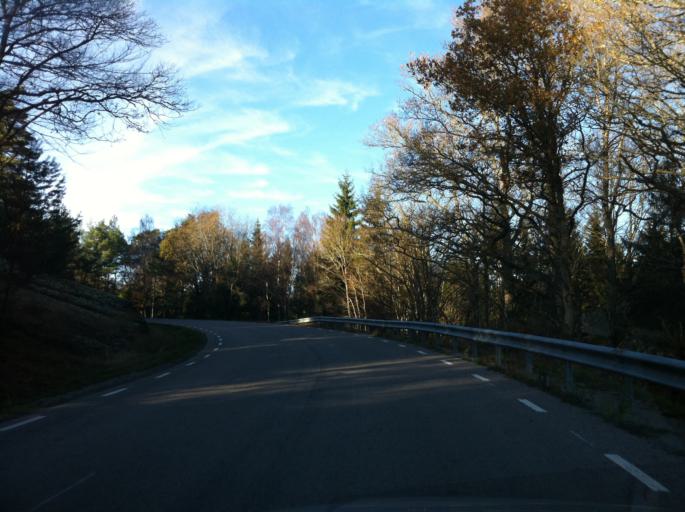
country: SE
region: Blekinge
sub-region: Ronneby Kommun
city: Brakne-Hoby
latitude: 56.1734
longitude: 15.1364
